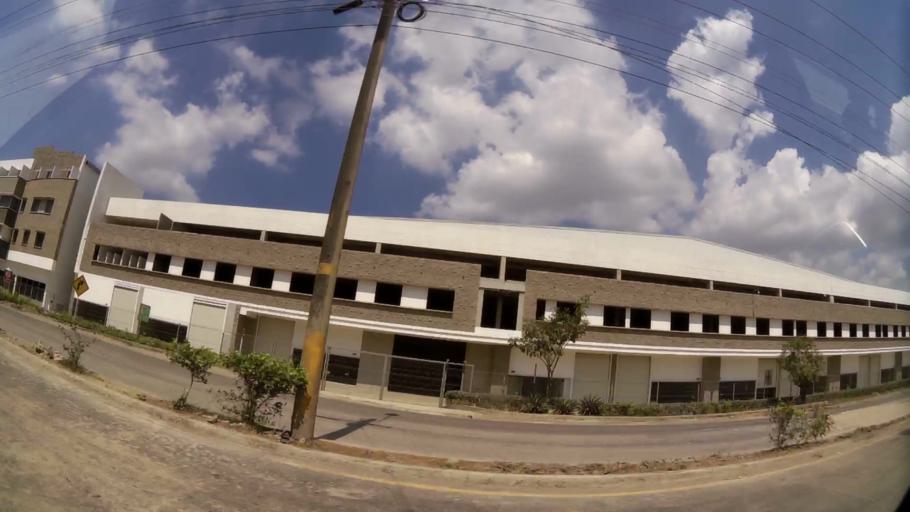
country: CO
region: Bolivar
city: Cartagena
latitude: 10.3424
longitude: -75.4928
